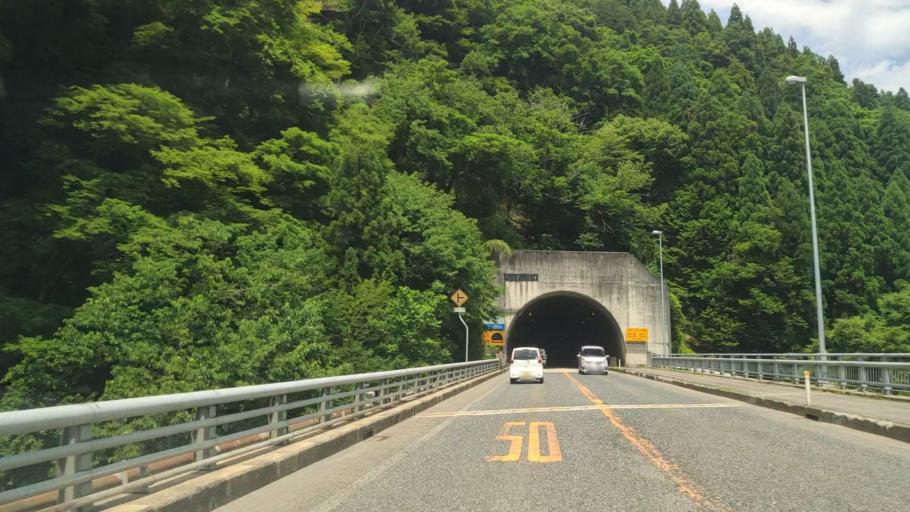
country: JP
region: Hyogo
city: Toyooka
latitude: 35.4911
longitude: 134.5686
